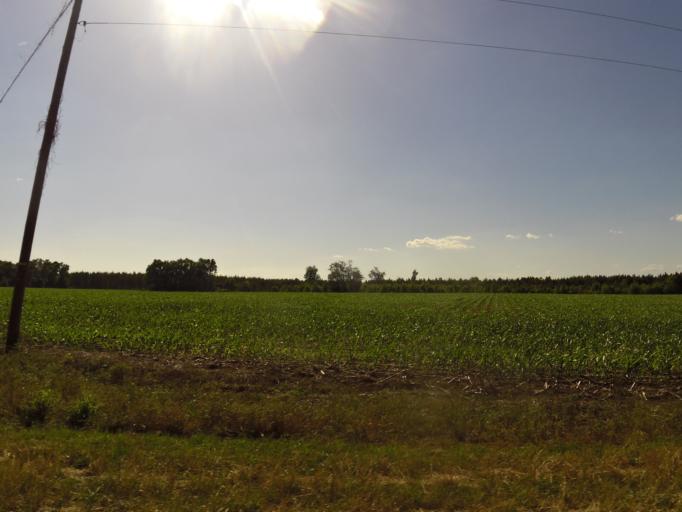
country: US
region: South Carolina
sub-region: Allendale County
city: Fairfax
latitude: 33.0051
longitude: -81.2190
